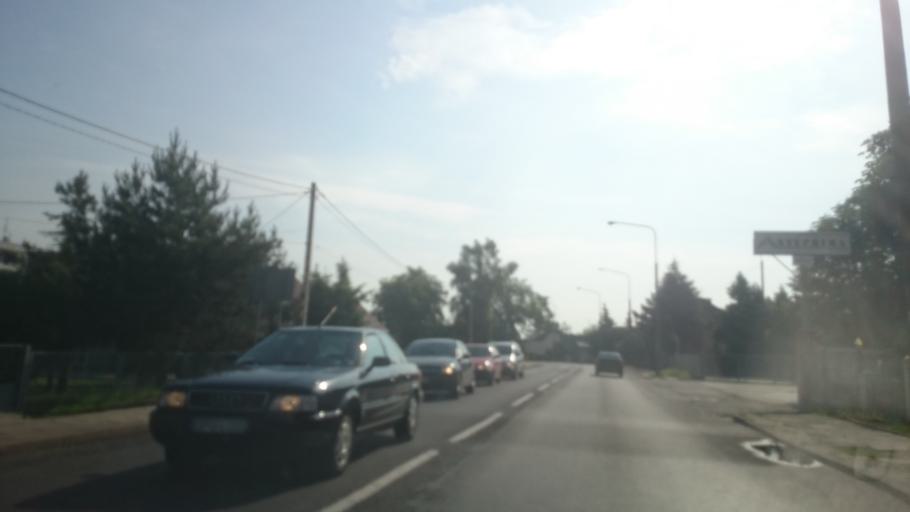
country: PL
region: Opole Voivodeship
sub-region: Powiat opolski
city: Opole
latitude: 50.6701
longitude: 17.9766
